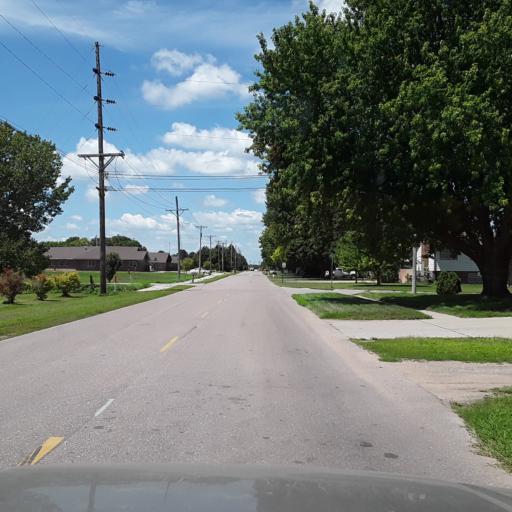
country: US
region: Nebraska
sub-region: Merrick County
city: Central City
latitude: 41.1048
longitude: -98.0097
